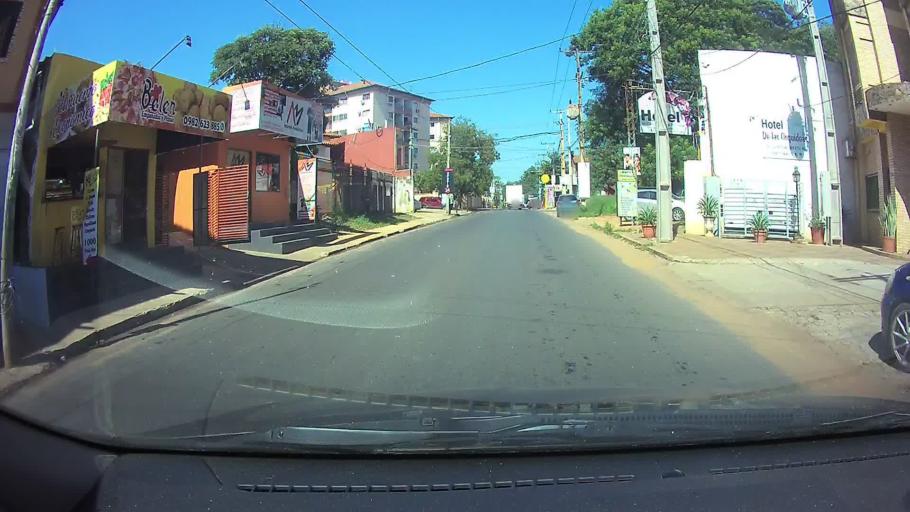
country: PY
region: Central
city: Fernando de la Mora
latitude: -25.3195
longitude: -57.5223
